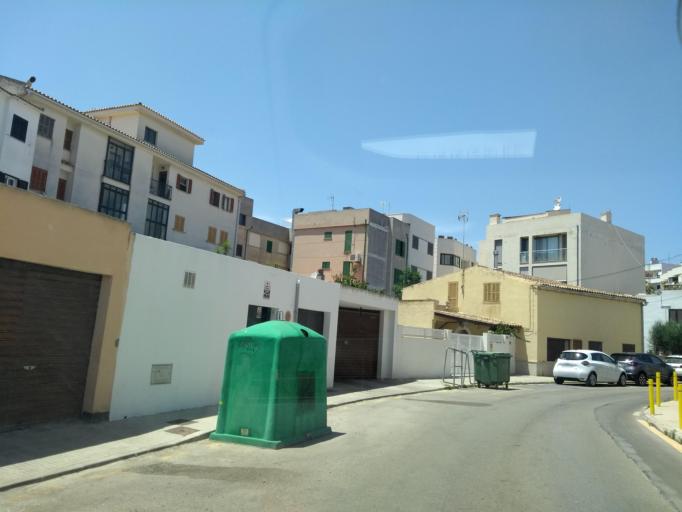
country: ES
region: Balearic Islands
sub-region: Illes Balears
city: Port d'Alcudia
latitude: 39.8389
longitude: 3.1394
